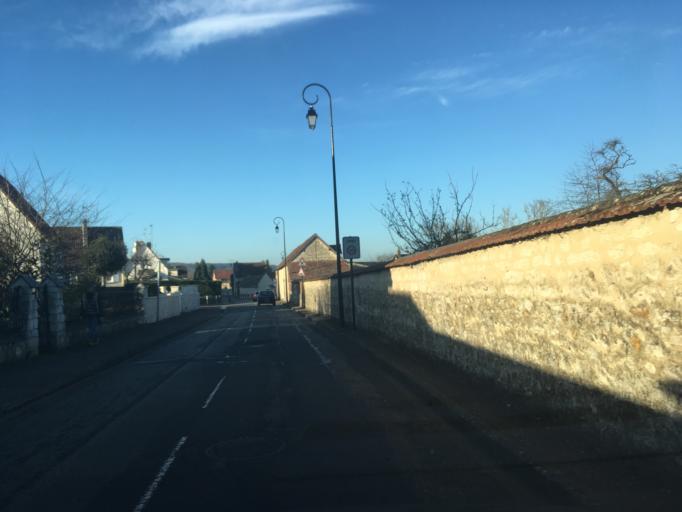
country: FR
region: Haute-Normandie
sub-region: Departement de l'Eure
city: Vernon
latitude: 49.0932
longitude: 1.4550
